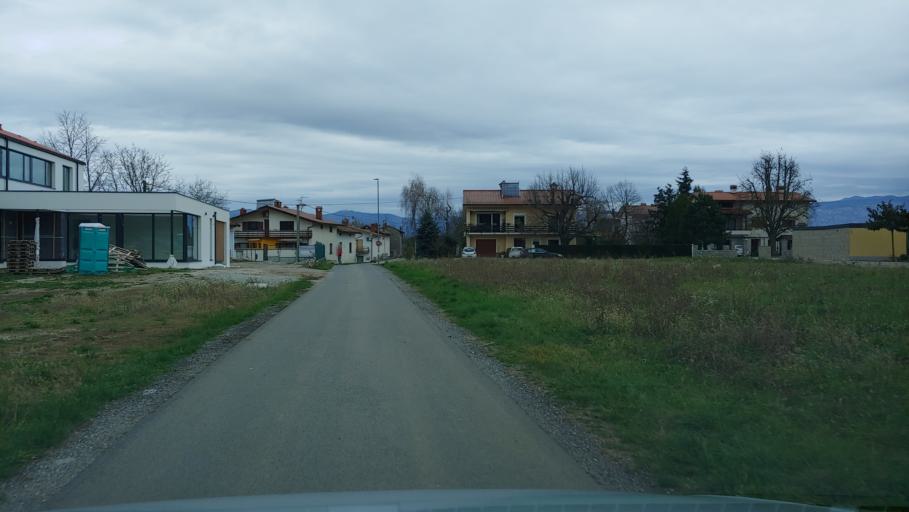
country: SI
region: Miren-Kostanjevica
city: Miren
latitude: 45.8916
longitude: 13.6142
